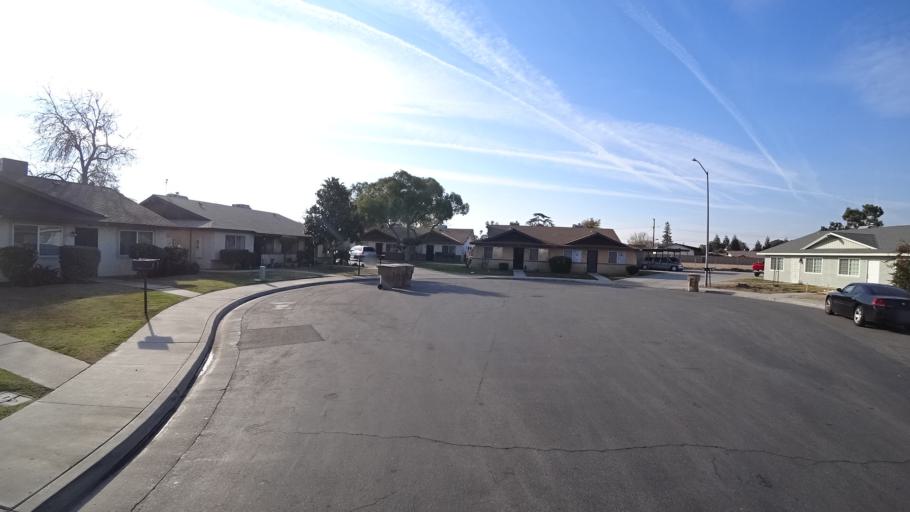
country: US
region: California
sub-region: Kern County
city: Bakersfield
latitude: 35.3210
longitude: -119.0307
